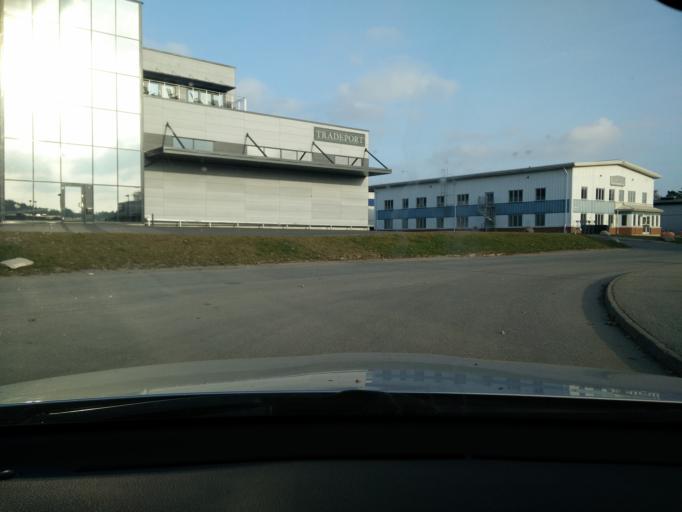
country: SE
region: Stockholm
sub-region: Taby Kommun
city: Taby
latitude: 59.4676
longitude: 18.1246
